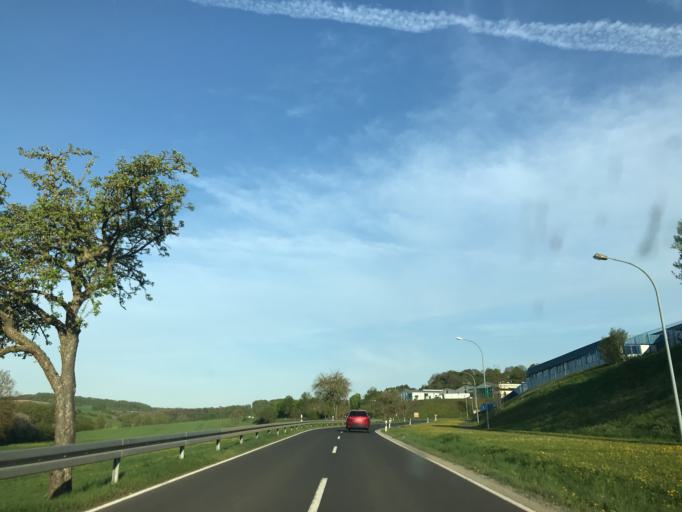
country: DE
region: Thuringia
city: Geisleden
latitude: 51.3443
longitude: 10.2075
